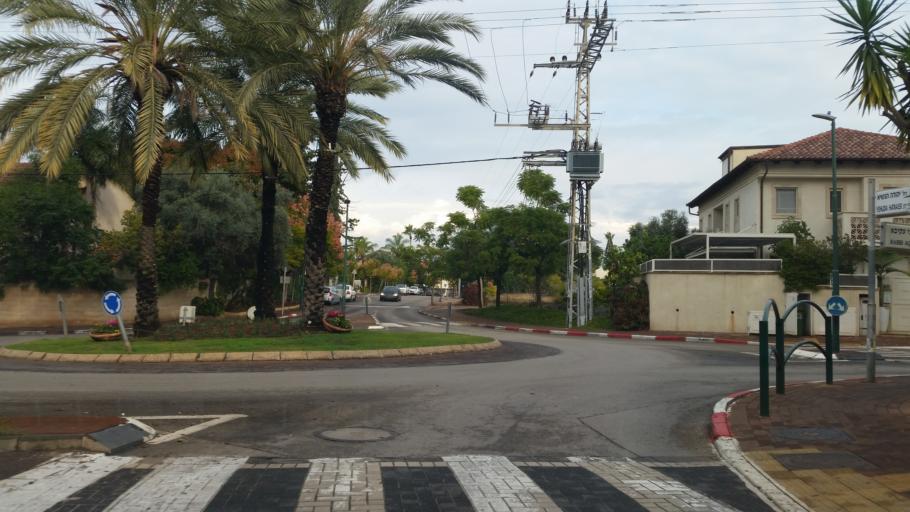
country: IL
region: Tel Aviv
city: Ramat HaSharon
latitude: 32.1536
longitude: 34.8476
